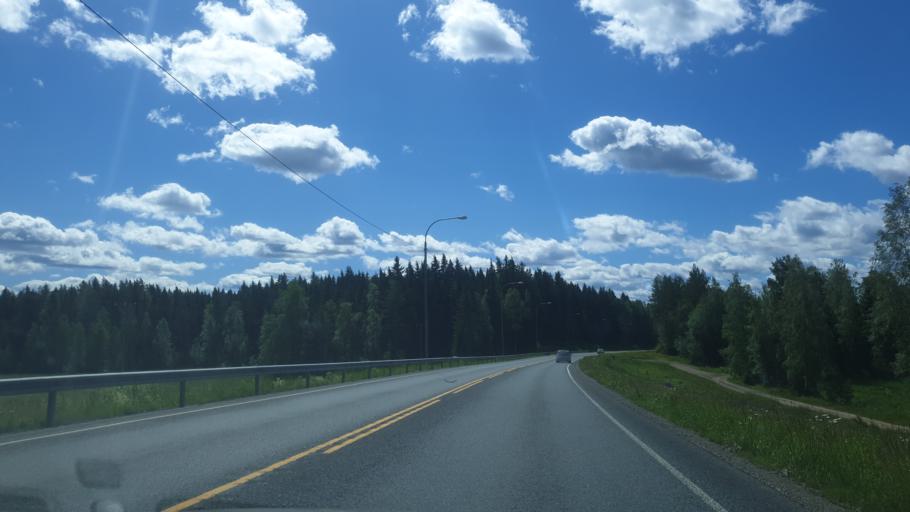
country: FI
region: Northern Savo
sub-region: Varkaus
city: Leppaevirta
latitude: 62.6085
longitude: 27.6230
